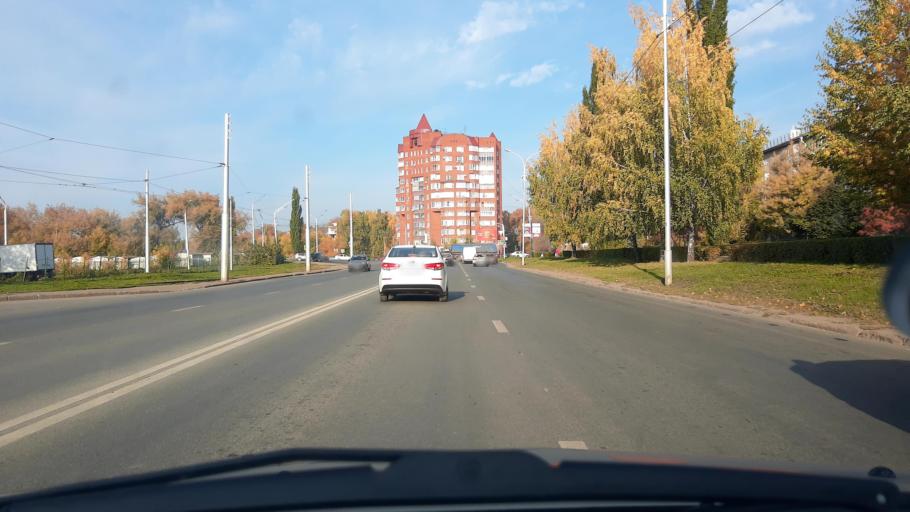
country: RU
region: Bashkortostan
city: Ufa
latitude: 54.8101
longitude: 56.0896
